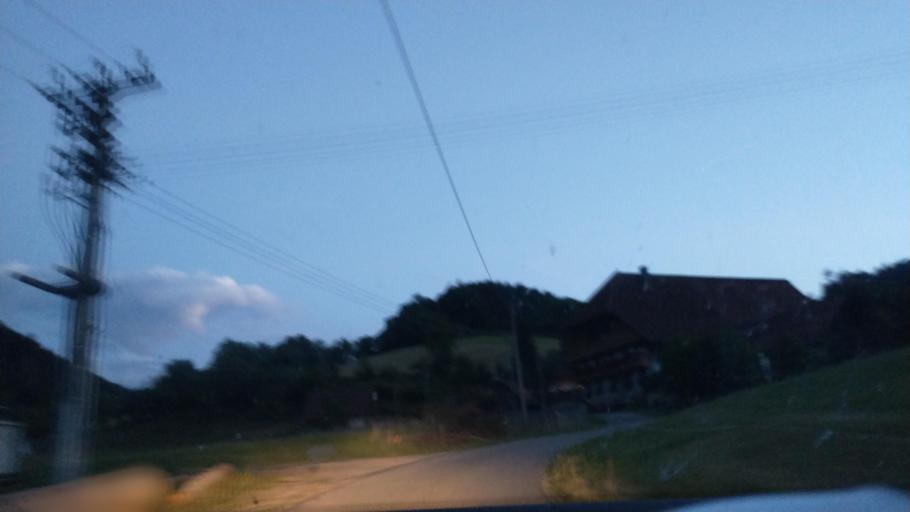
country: DE
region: Baden-Wuerttemberg
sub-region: Freiburg Region
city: Biberach
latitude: 48.3131
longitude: 7.9975
